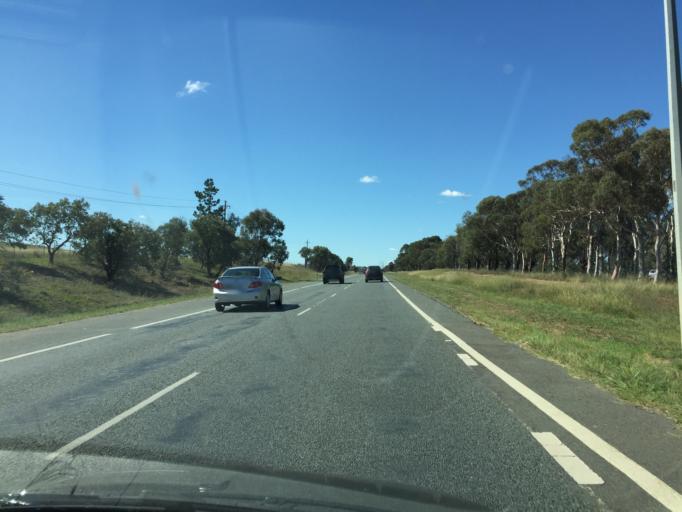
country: AU
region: Australian Capital Territory
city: Macarthur
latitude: -35.3793
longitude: 149.1697
